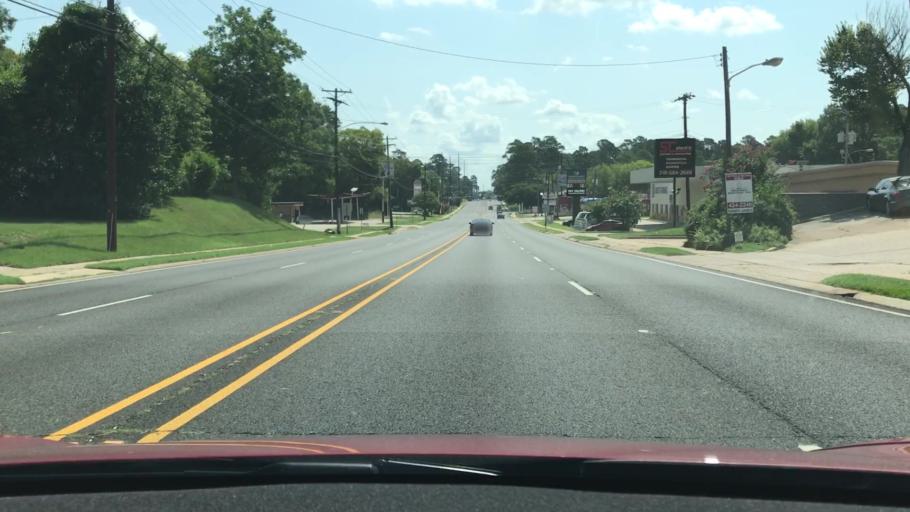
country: US
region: Louisiana
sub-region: Bossier Parish
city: Bossier City
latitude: 32.4422
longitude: -93.7422
